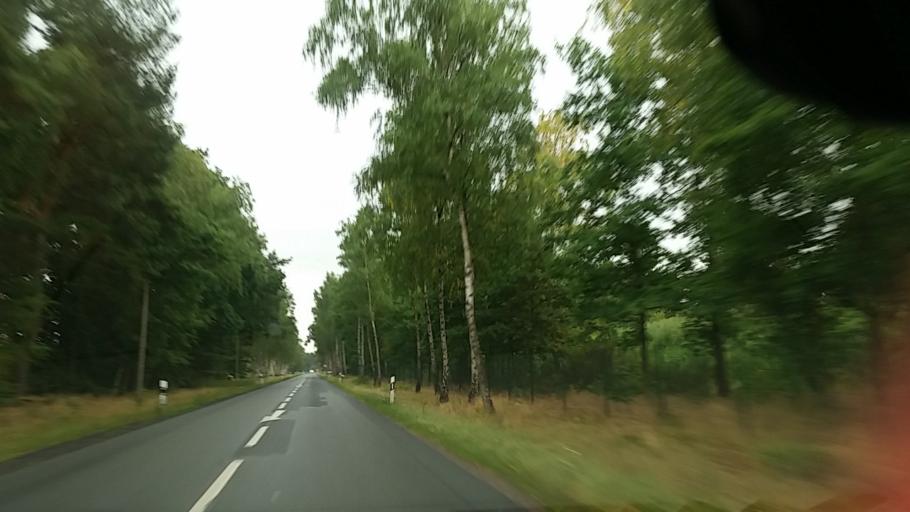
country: DE
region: Lower Saxony
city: Sassenburg
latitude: 52.5625
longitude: 10.6765
